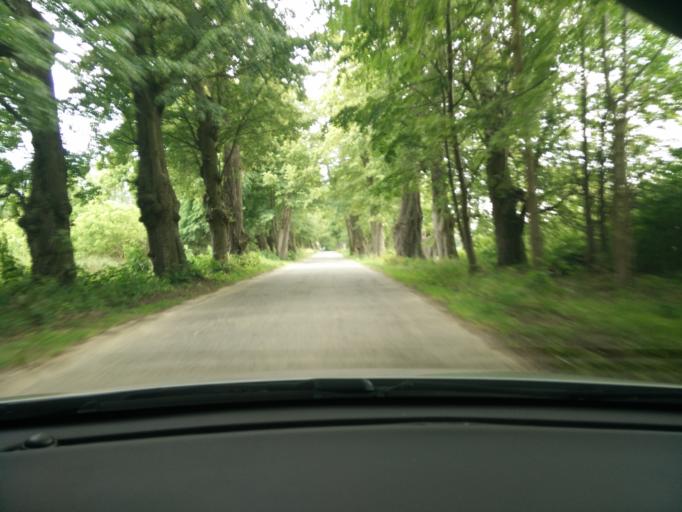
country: PL
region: Pomeranian Voivodeship
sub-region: Powiat pucki
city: Mrzezino
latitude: 54.6826
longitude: 18.4614
